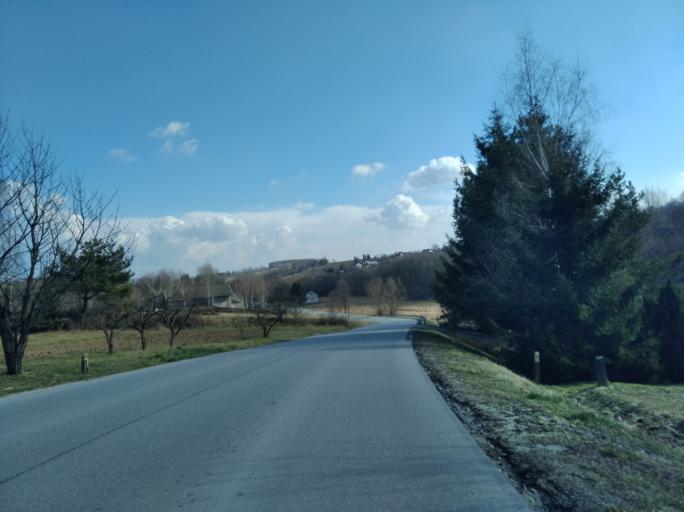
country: PL
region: Subcarpathian Voivodeship
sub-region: Powiat strzyzowski
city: Frysztak
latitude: 49.8465
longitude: 21.5577
